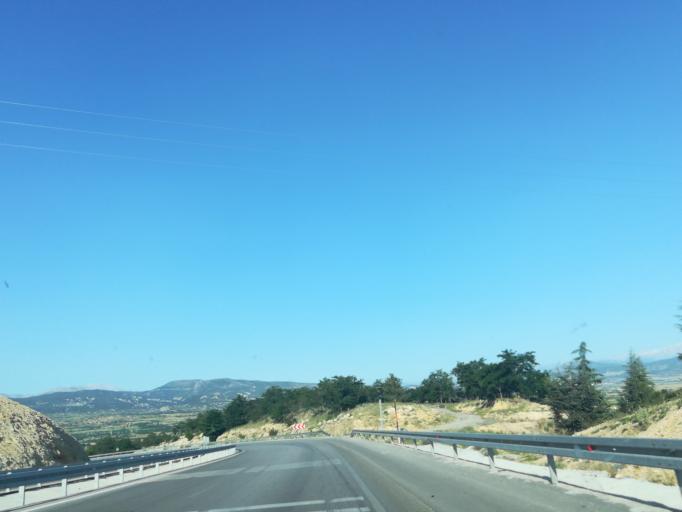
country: TR
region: Isparta
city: Keciborlu
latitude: 37.9163
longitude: 30.2911
